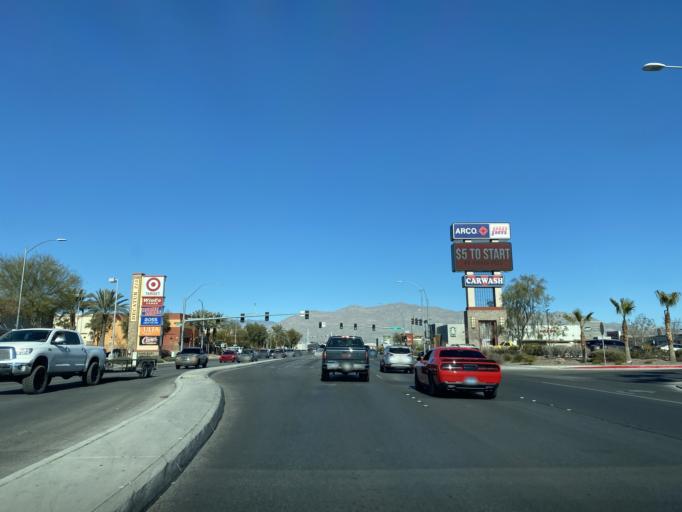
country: US
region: Nevada
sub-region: Clark County
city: North Las Vegas
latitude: 36.2700
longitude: -115.2067
